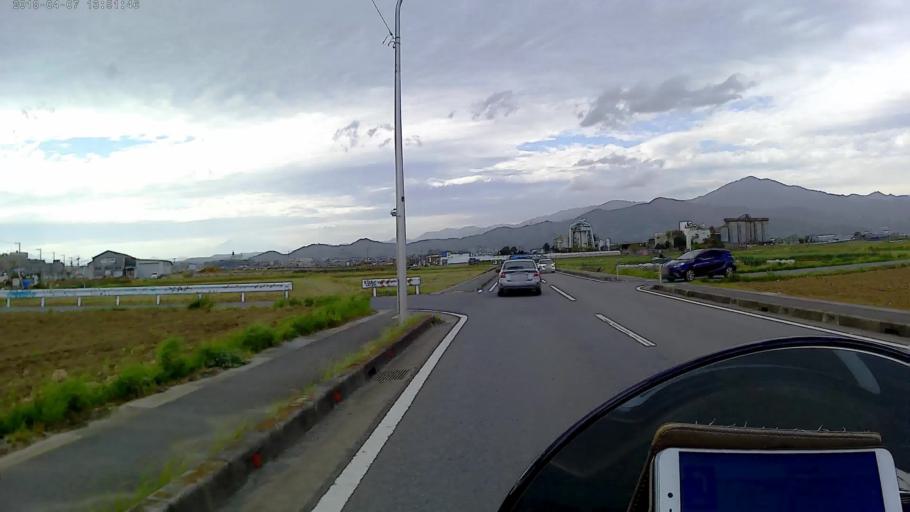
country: JP
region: Kanagawa
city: Isehara
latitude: 35.3663
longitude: 139.3024
